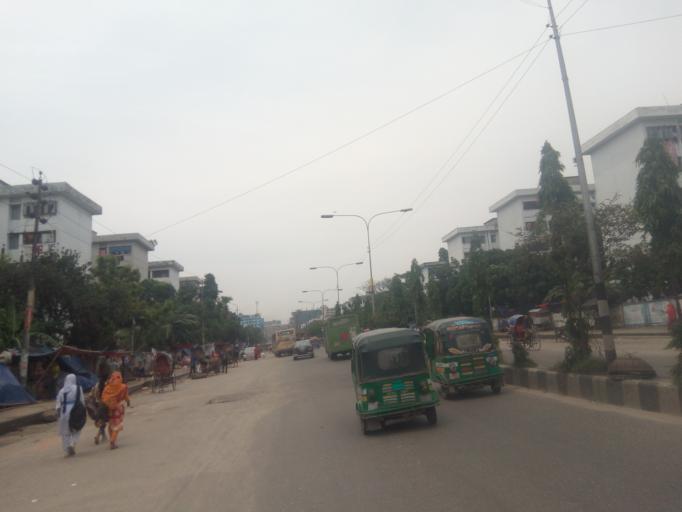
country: BD
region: Dhaka
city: Azimpur
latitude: 23.7899
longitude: 90.3538
